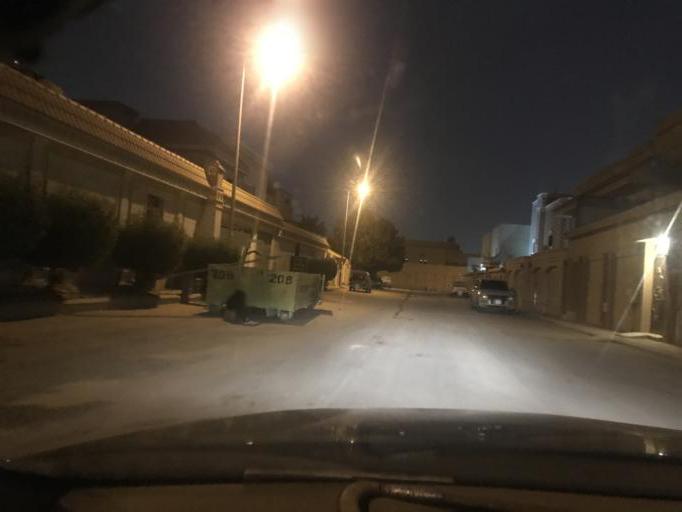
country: SA
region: Ar Riyad
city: Riyadh
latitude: 24.7504
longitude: 46.7752
